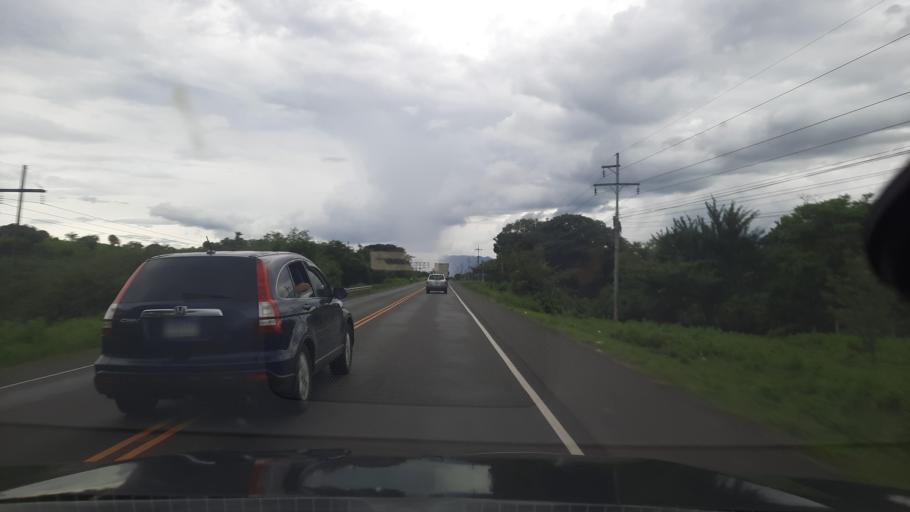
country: HN
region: Choluteca
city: Ciudad Choluteca
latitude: 13.3417
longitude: -87.2503
